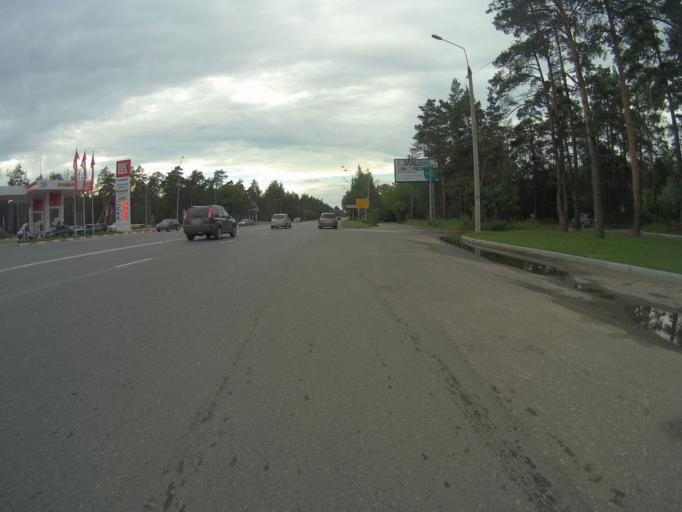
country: RU
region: Vladimir
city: Kommunar
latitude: 56.0964
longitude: 40.4468
